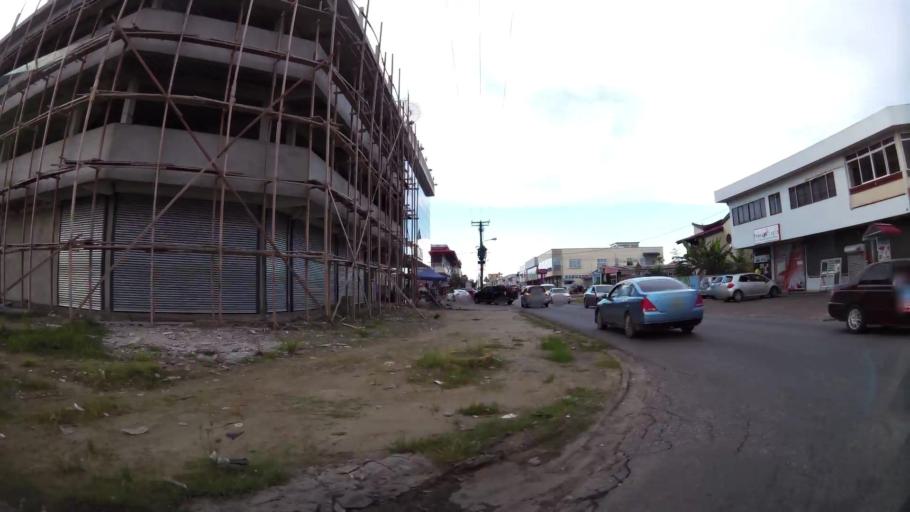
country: SR
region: Paramaribo
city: Paramaribo
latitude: 5.8476
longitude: -55.1408
